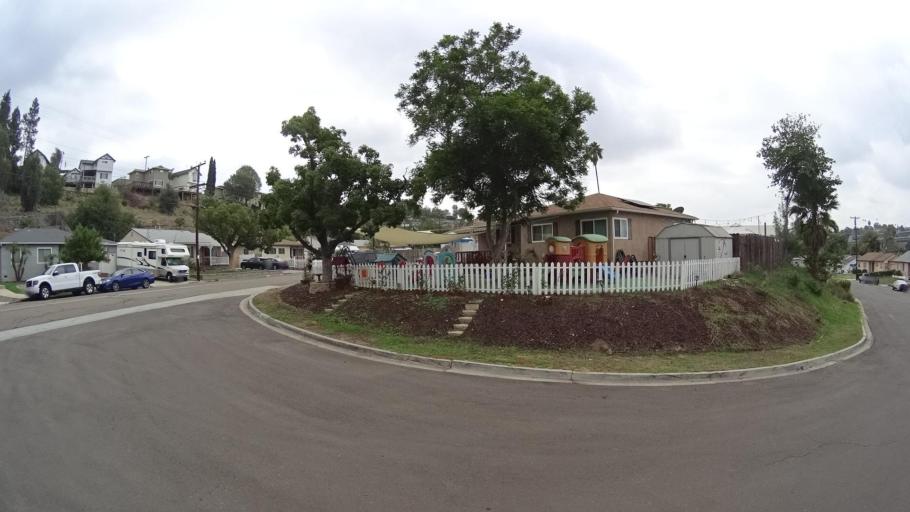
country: US
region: California
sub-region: San Diego County
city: Spring Valley
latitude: 32.7492
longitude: -117.0126
